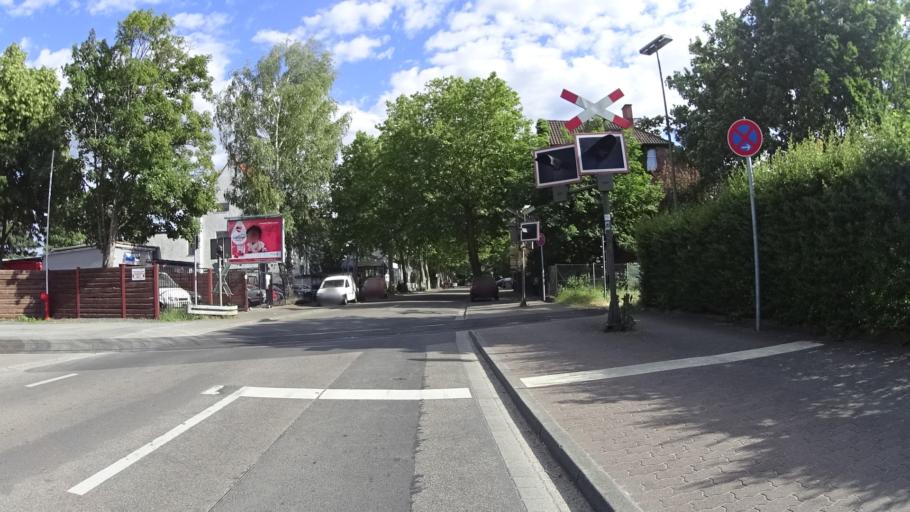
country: DE
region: Hesse
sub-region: Regierungsbezirk Darmstadt
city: Hanau am Main
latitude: 50.1127
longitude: 8.9374
